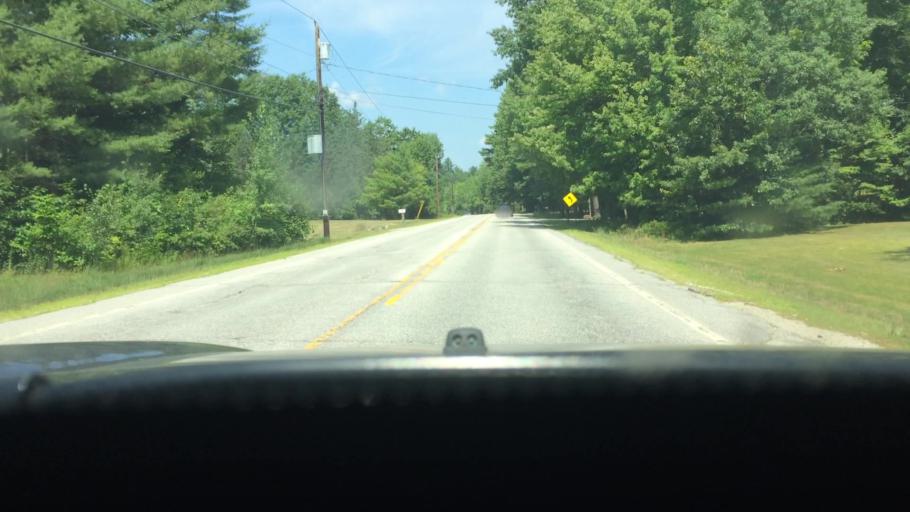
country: US
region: Maine
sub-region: Androscoggin County
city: Mechanic Falls
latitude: 44.1128
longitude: -70.4228
